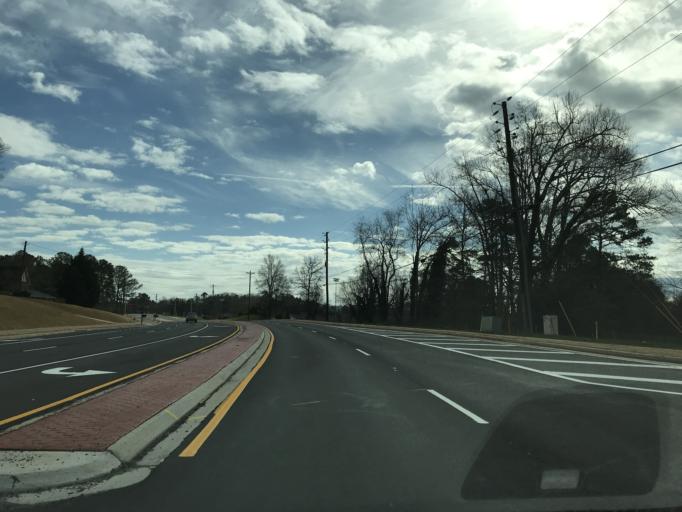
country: US
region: Georgia
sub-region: Forsyth County
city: Cumming
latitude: 34.1207
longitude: -84.1659
